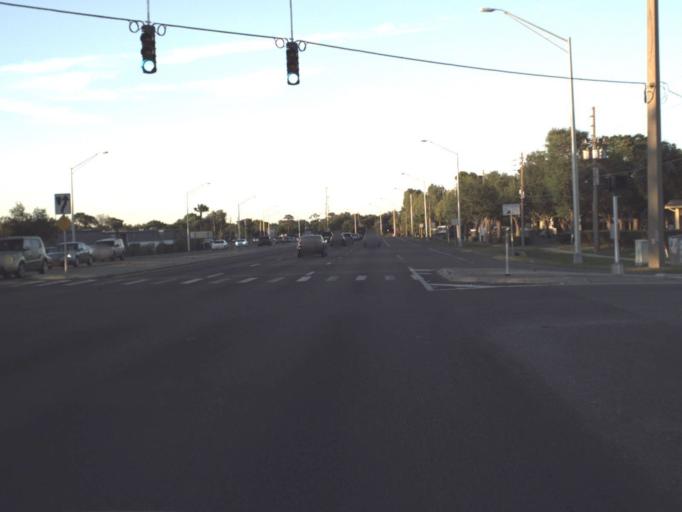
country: US
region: Florida
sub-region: Orange County
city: Union Park
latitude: 28.5788
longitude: -81.3089
